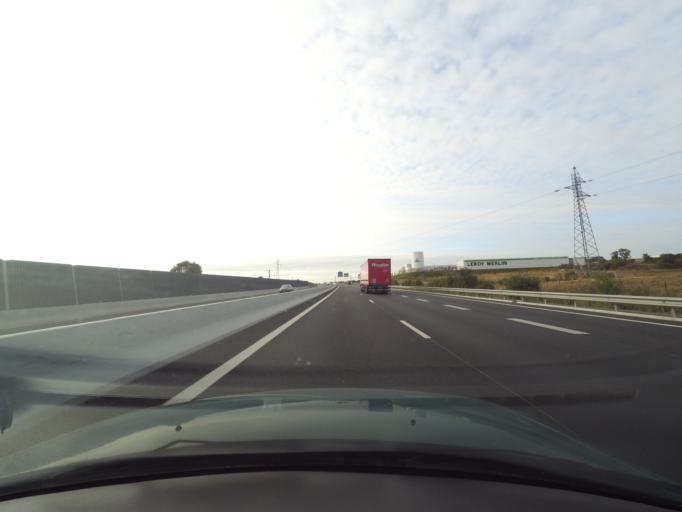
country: FR
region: Pays de la Loire
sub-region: Departement de Maine-et-Loire
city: La Seguiniere
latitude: 47.0416
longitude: -0.9104
